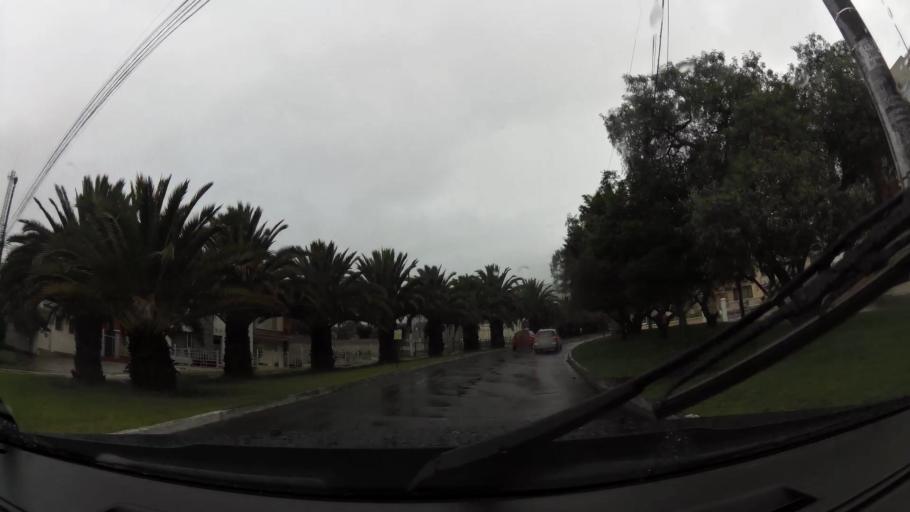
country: EC
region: Pichincha
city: Quito
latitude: -0.1029
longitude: -78.5010
